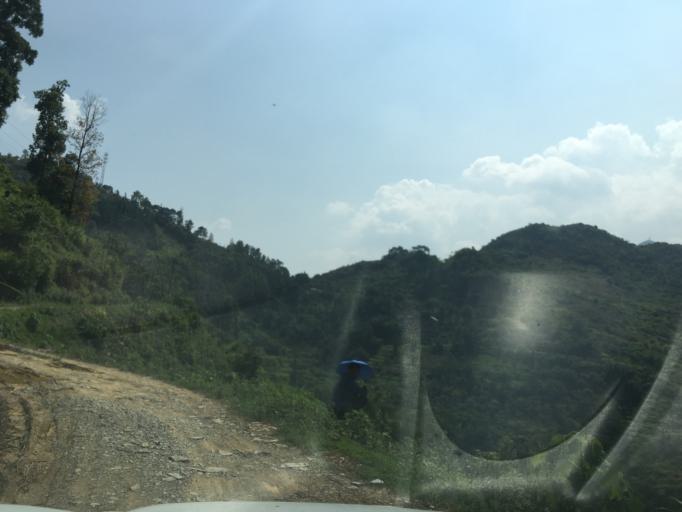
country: CN
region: Guangxi Zhuangzu Zizhiqu
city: Xinzhou
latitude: 24.9908
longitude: 105.7387
